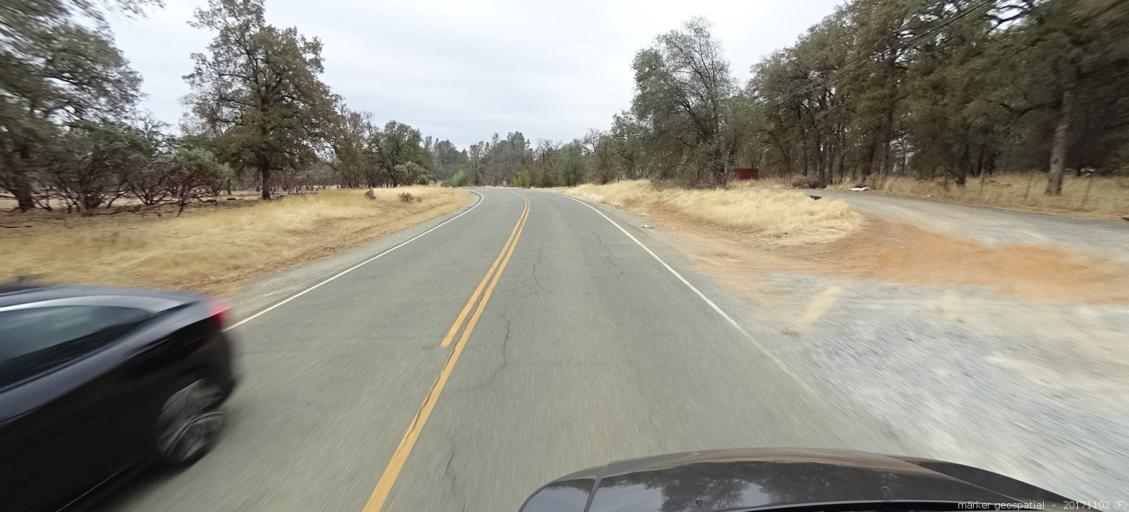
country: US
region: California
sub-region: Shasta County
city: Shasta Lake
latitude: 40.6754
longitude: -122.3216
